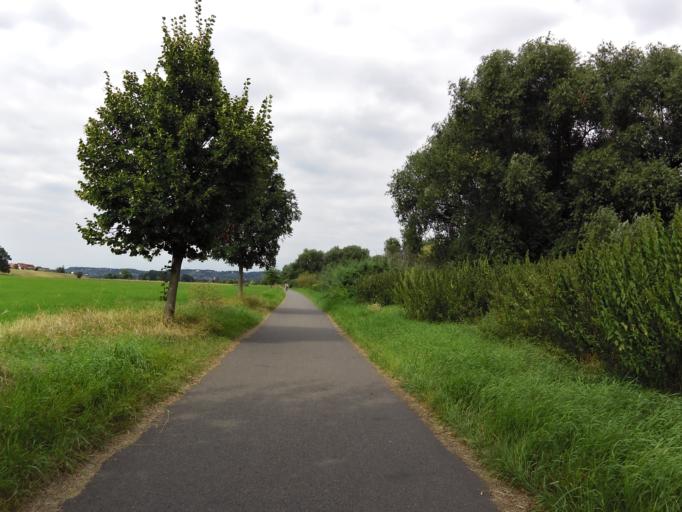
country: DE
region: Saxony
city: Radebeul
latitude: 51.0797
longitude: 13.6670
